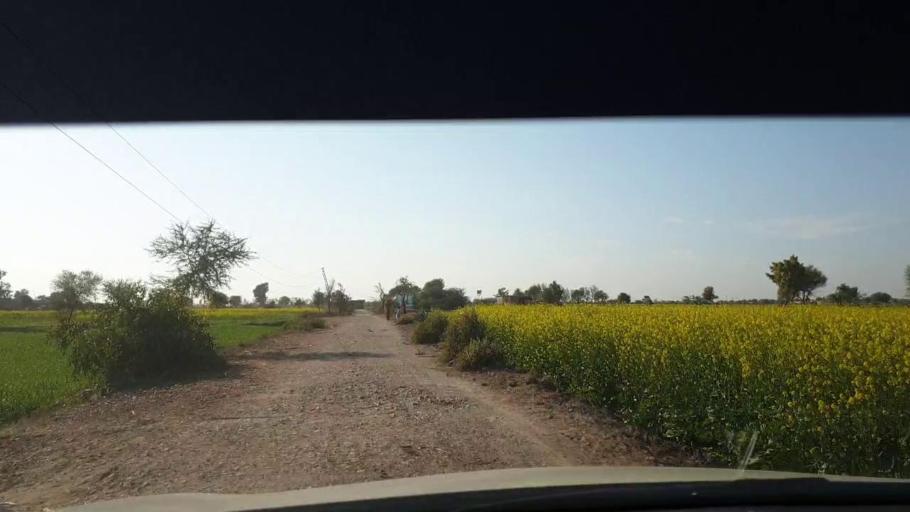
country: PK
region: Sindh
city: Berani
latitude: 25.8055
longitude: 68.9316
